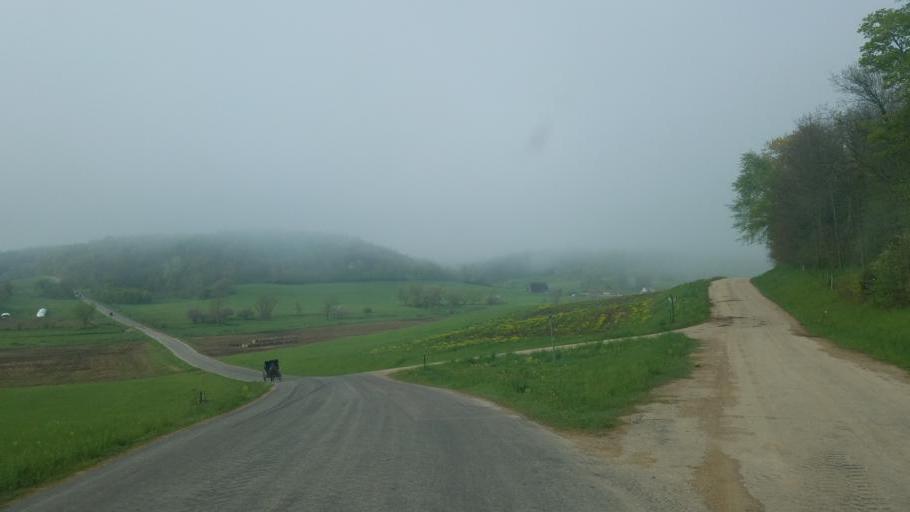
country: US
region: Wisconsin
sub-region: Vernon County
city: Hillsboro
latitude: 43.6124
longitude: -90.4061
